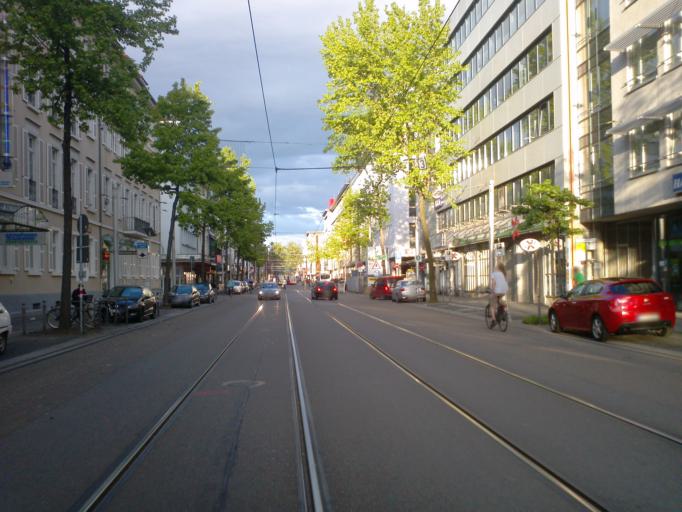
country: DE
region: Baden-Wuerttemberg
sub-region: Karlsruhe Region
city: Karlsruhe
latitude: 49.0101
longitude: 8.3913
